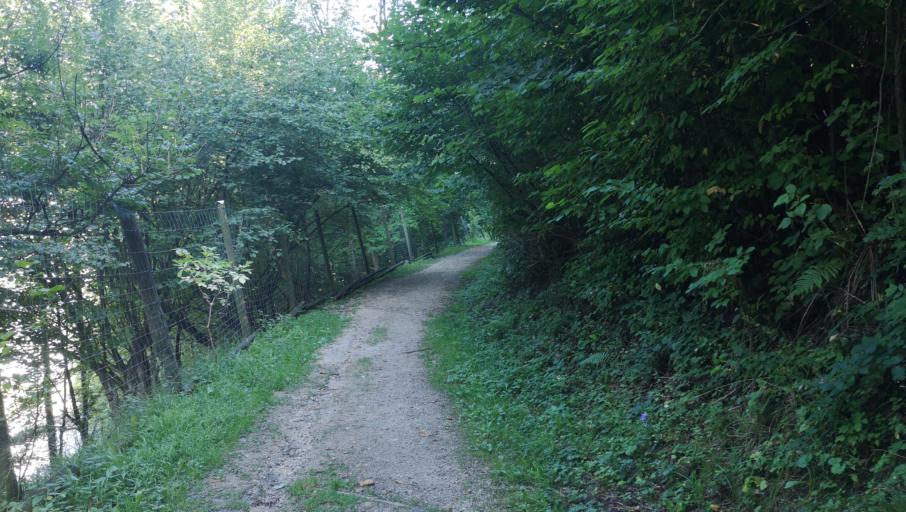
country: AT
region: Lower Austria
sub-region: Waidhofen an der Ybbs Stadt
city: Waidhofen an der Ybbs
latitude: 47.9560
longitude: 14.7757
